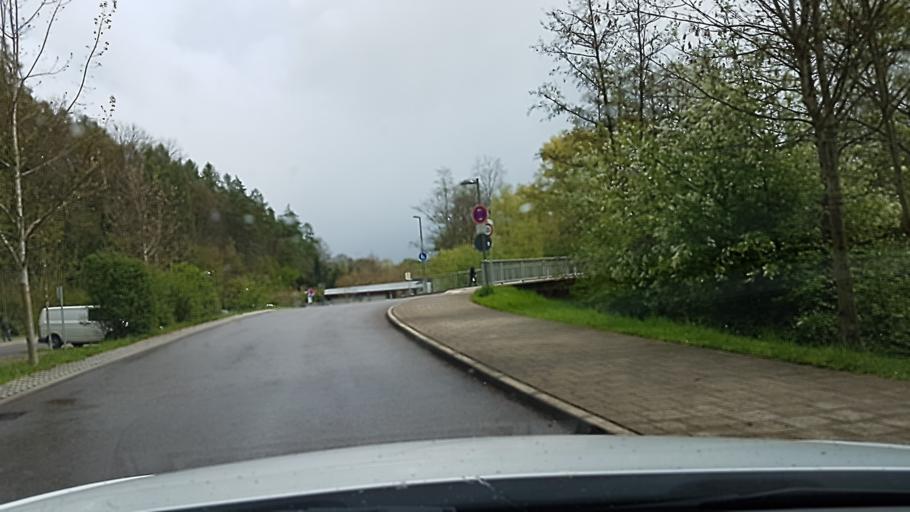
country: DE
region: Baden-Wuerttemberg
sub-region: Regierungsbezirk Stuttgart
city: Backnang
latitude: 48.9520
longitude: 9.4548
